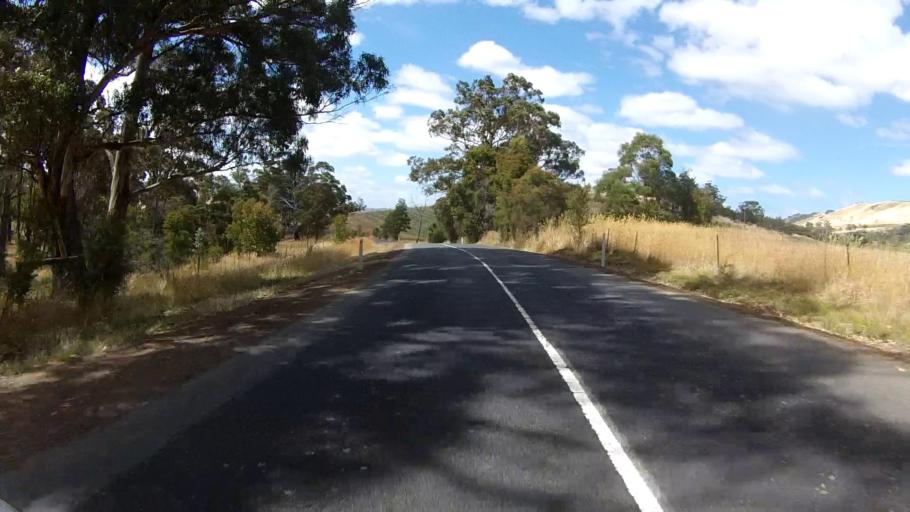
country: AU
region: Tasmania
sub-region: Sorell
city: Sorell
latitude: -42.7458
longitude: 147.4859
